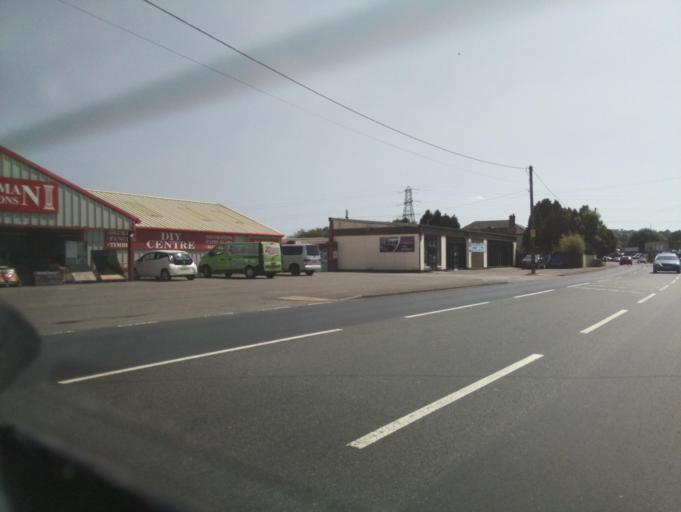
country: GB
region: Wales
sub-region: Caerphilly County Borough
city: Pengam
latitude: 51.6669
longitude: -3.2296
